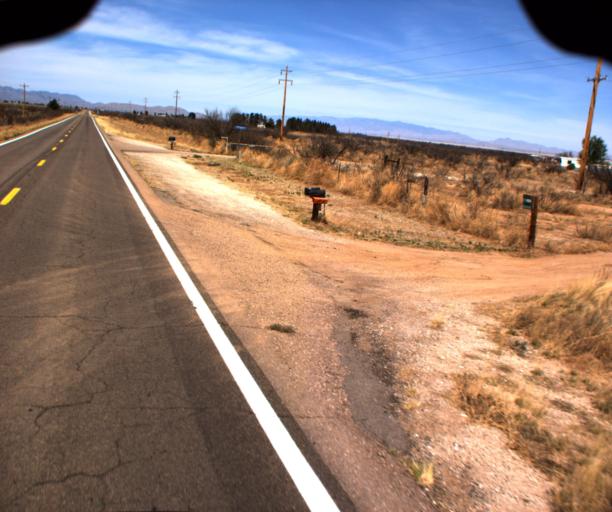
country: US
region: Arizona
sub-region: Cochise County
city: Willcox
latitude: 32.0895
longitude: -109.9059
